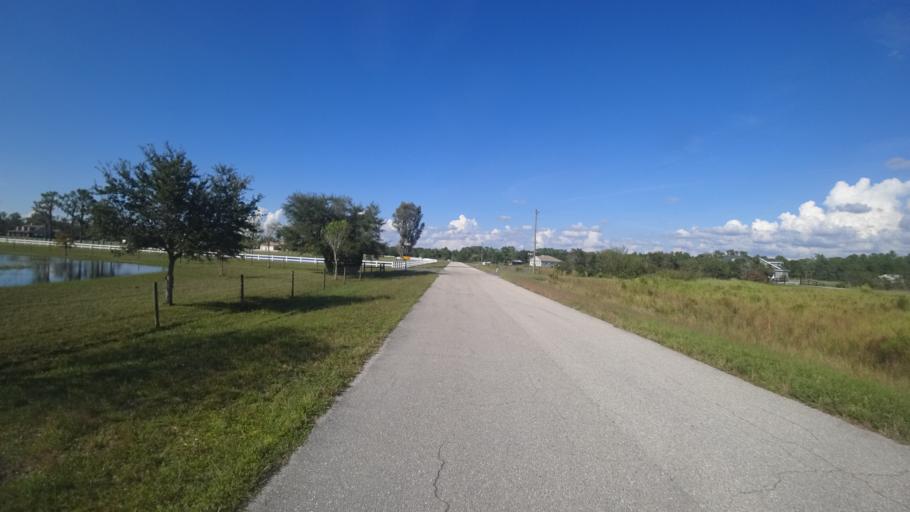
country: US
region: Florida
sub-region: Sarasota County
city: Lake Sarasota
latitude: 27.3935
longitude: -82.2835
